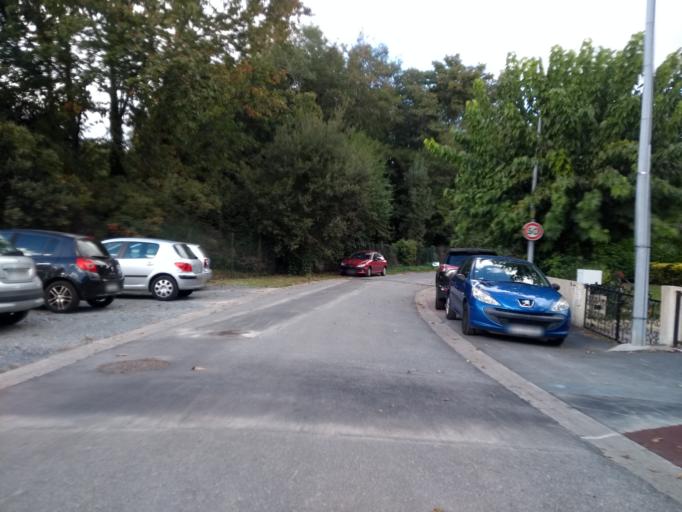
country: FR
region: Aquitaine
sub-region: Departement de la Gironde
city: Canejan
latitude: 44.7589
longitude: -0.6390
